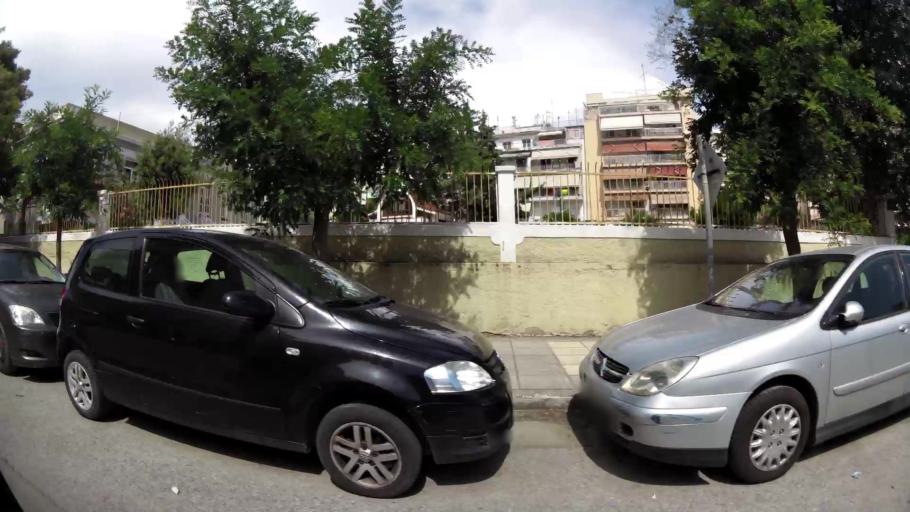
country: GR
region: Central Macedonia
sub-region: Nomos Thessalonikis
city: Triandria
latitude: 40.6035
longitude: 22.9587
